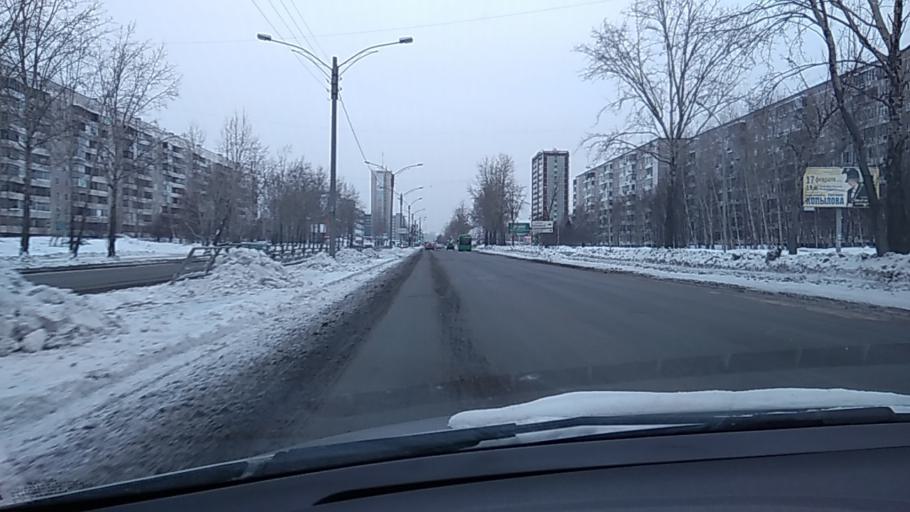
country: RU
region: Sverdlovsk
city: Sovkhoznyy
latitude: 56.8076
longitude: 60.5434
